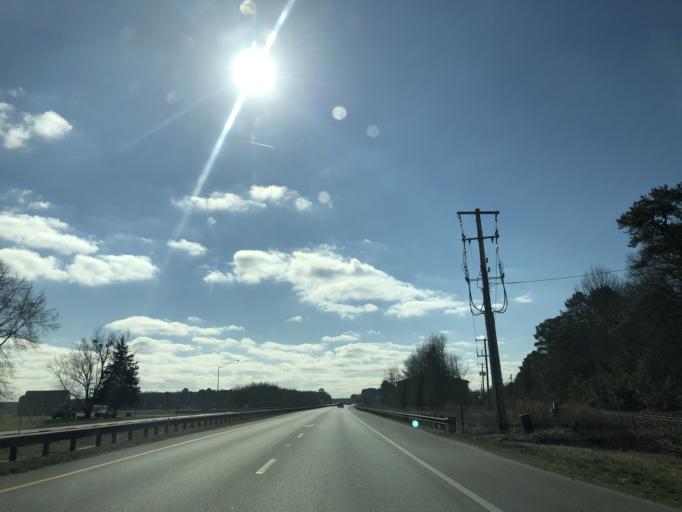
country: US
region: Delaware
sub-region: Sussex County
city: Selbyville
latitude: 38.4346
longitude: -75.2229
